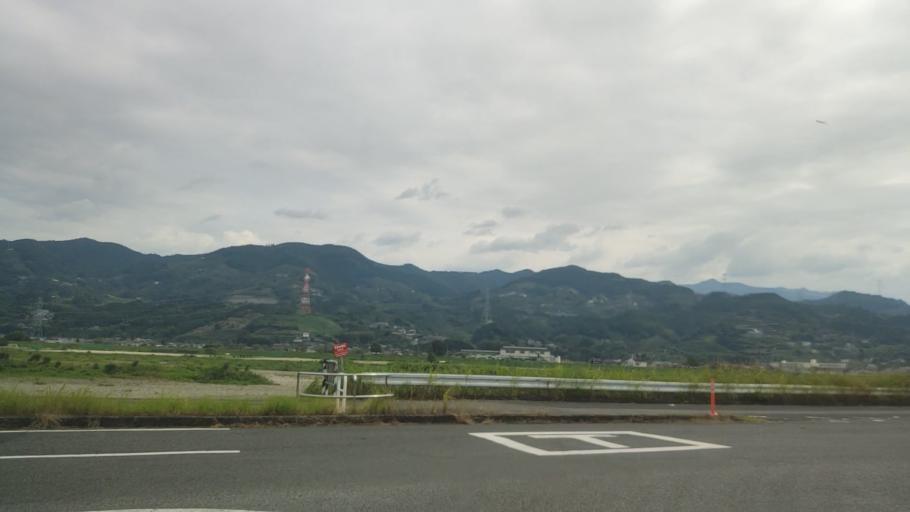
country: JP
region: Wakayama
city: Hashimoto
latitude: 34.3098
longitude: 135.5864
